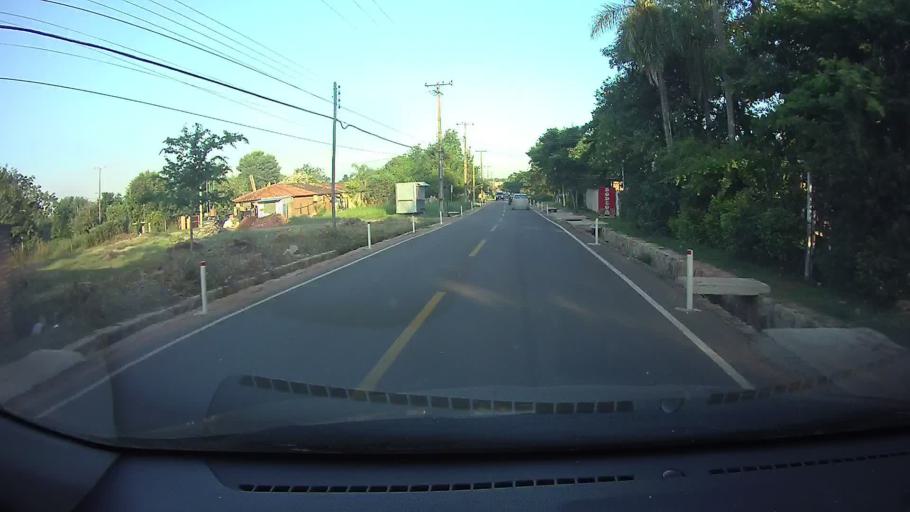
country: PY
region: Central
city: Limpio
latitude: -25.2513
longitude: -57.4961
